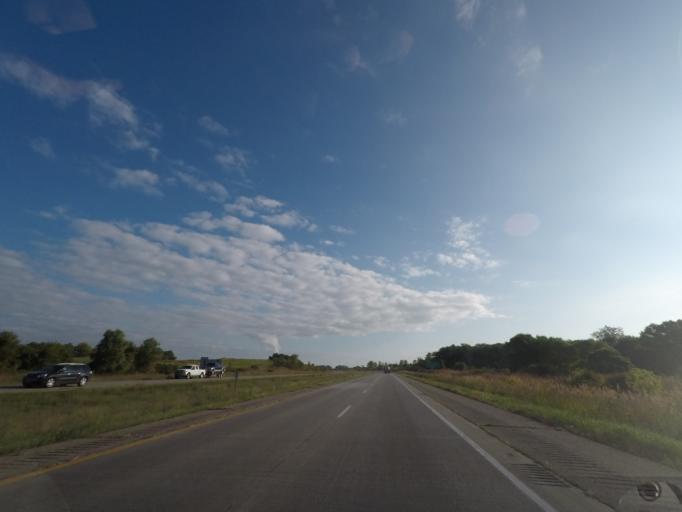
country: US
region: Iowa
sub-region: Polk County
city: Pleasant Hill
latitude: 41.5846
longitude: -93.5046
